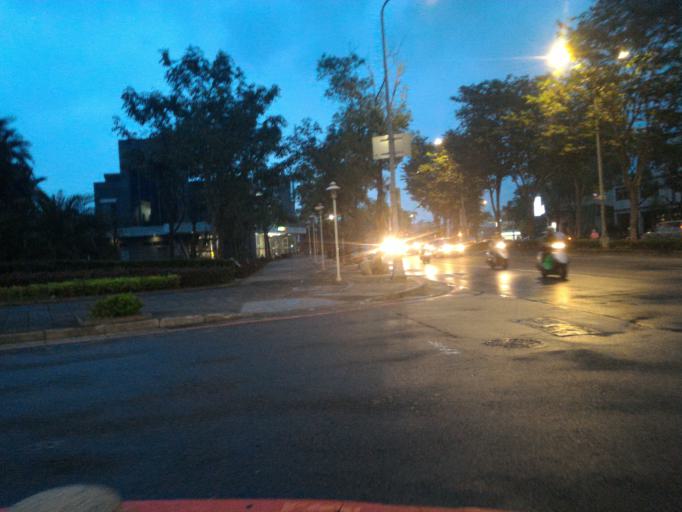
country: TW
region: Taiwan
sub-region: Taoyuan
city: Taoyuan
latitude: 24.9501
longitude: 121.3859
